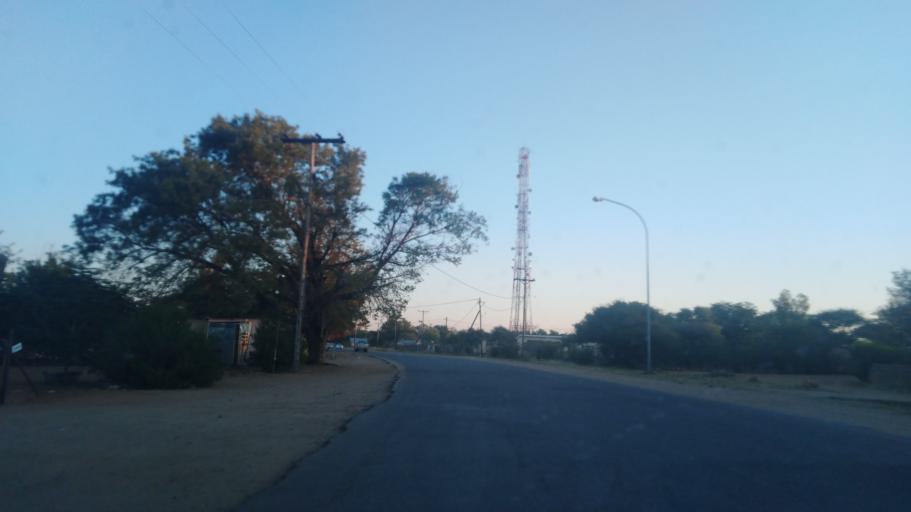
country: BW
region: Central
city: Mahalapye
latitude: -23.1143
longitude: 26.8297
